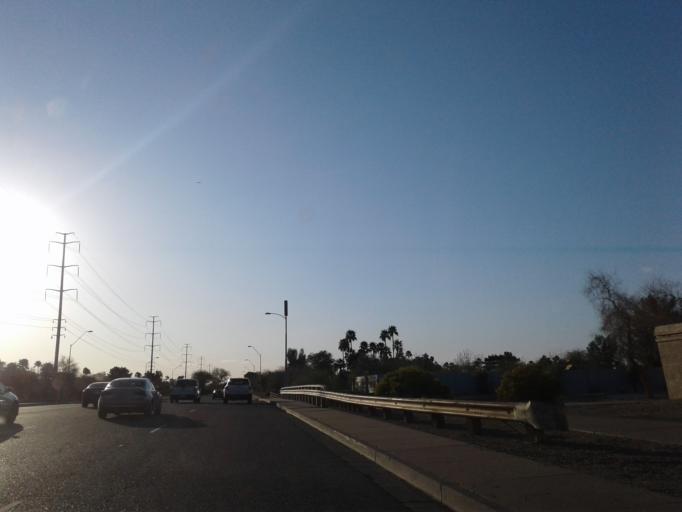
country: US
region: Arizona
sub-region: Maricopa County
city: Scottsdale
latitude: 33.5826
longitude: -111.8643
